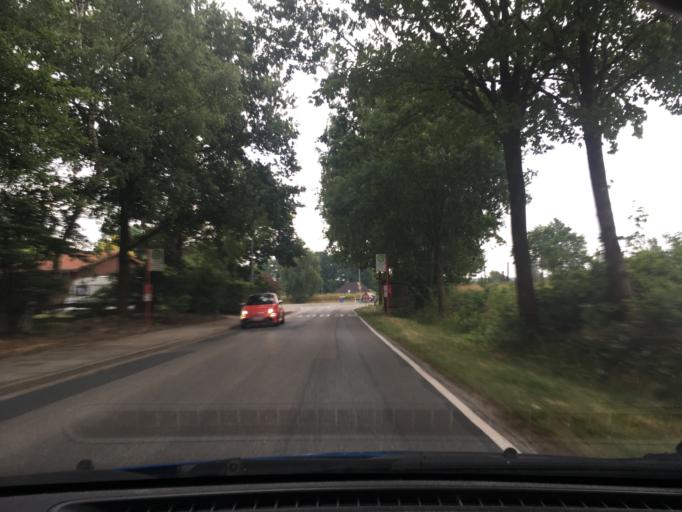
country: DE
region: Lower Saxony
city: Kakenstorf
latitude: 53.3205
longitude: 9.7865
